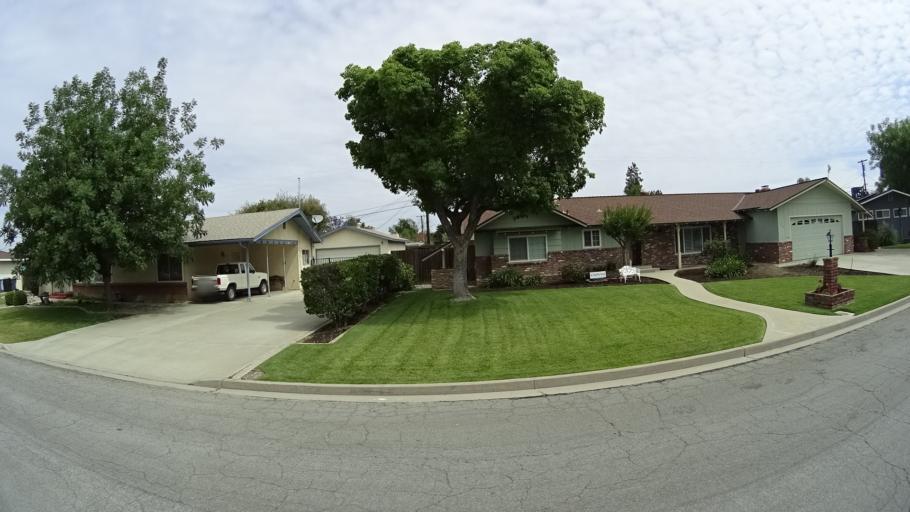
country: US
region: California
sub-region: Kings County
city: Hanford
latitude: 36.3547
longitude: -119.6436
